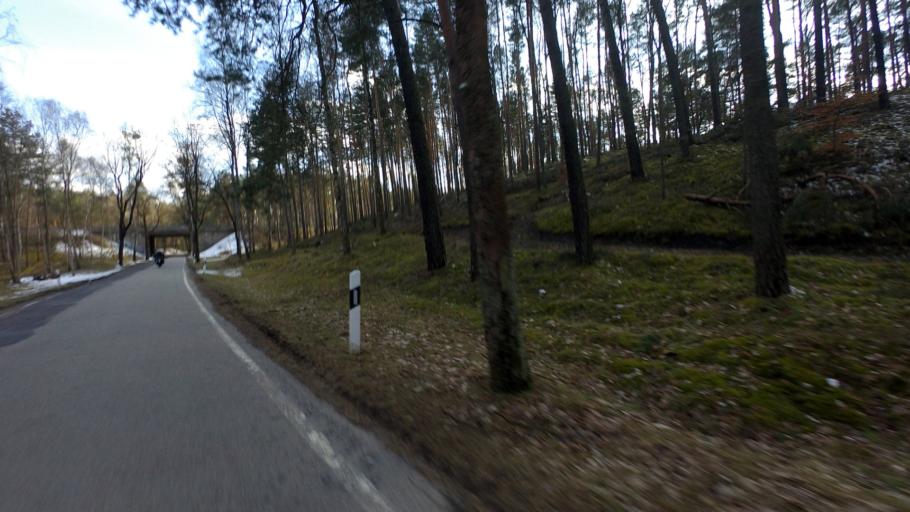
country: DE
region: Brandenburg
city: Marienwerder
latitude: 52.7968
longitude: 13.5983
